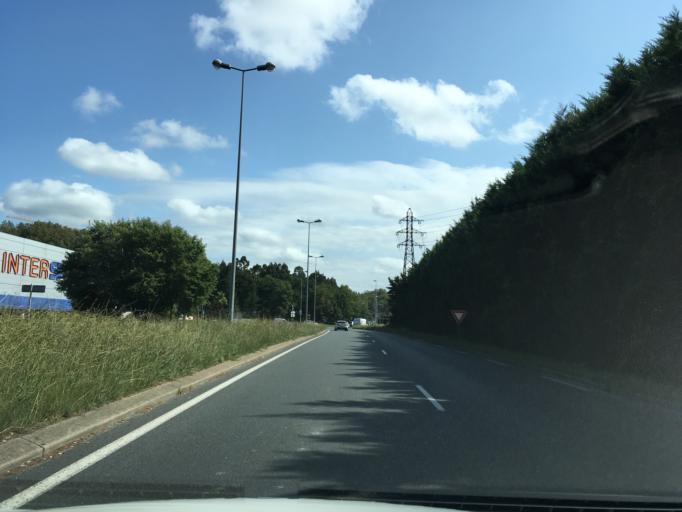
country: FR
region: Aquitaine
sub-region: Departement des Pyrenees-Atlantiques
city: Bayonne
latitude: 43.4896
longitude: -1.4927
